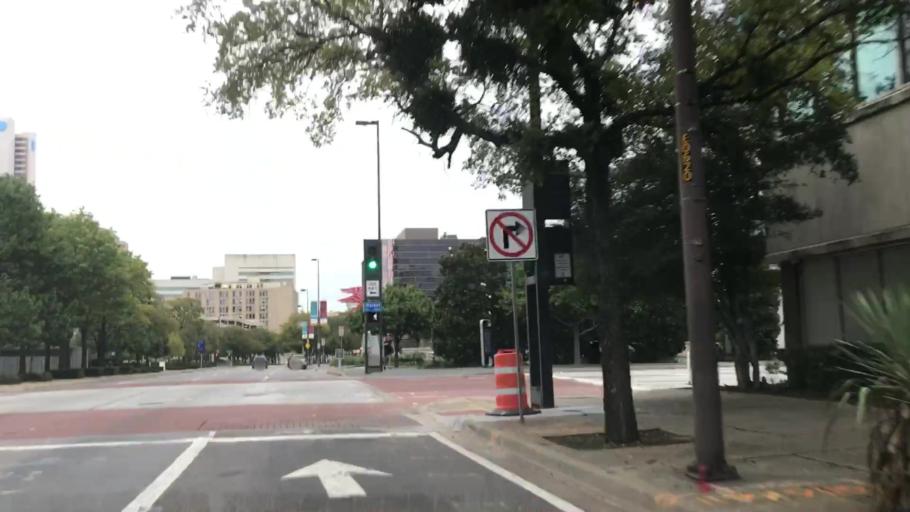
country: US
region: Texas
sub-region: Dallas County
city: Dallas
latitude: 32.7761
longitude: -96.8056
